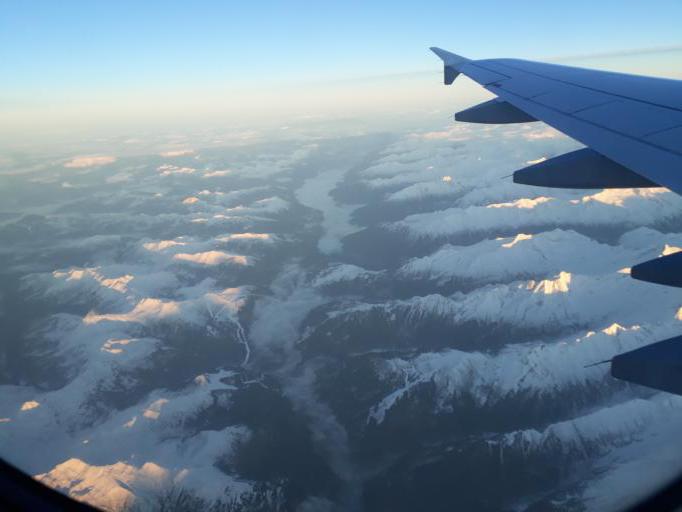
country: AT
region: Tyrol
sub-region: Politischer Bezirk Schwaz
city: Ramsau im Zillertal
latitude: 47.1966
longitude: 11.8929
